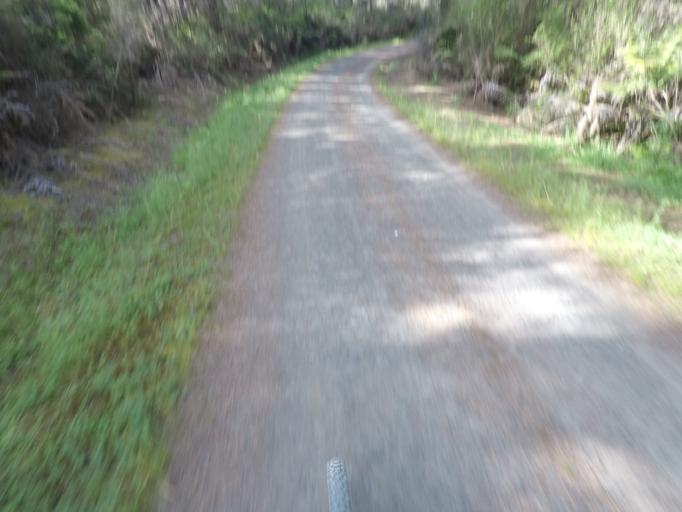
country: NZ
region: Auckland
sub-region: Auckland
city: Muriwai Beach
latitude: -36.7426
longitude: 174.5715
